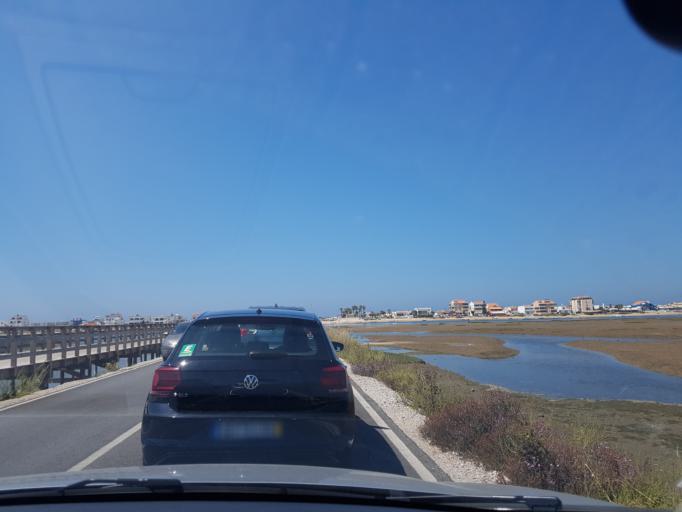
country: PT
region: Faro
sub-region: Faro
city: Faro
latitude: 37.0114
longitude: -7.9912
